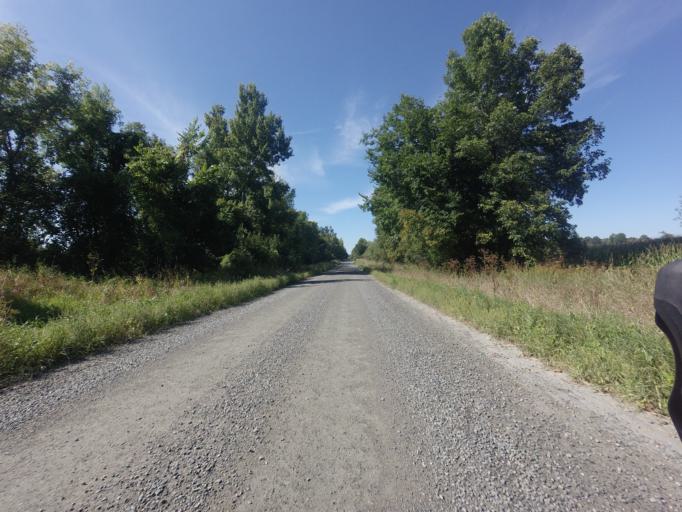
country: CA
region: Ontario
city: Perth
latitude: 44.9566
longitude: -76.3334
